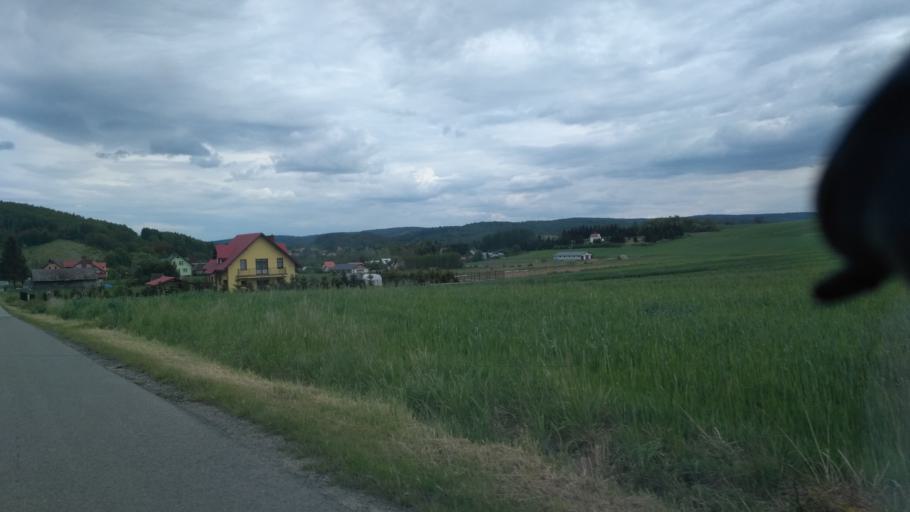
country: PL
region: Subcarpathian Voivodeship
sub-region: Powiat przemyski
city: Przedmiescie Dubieckie
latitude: 49.8347
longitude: 22.3179
